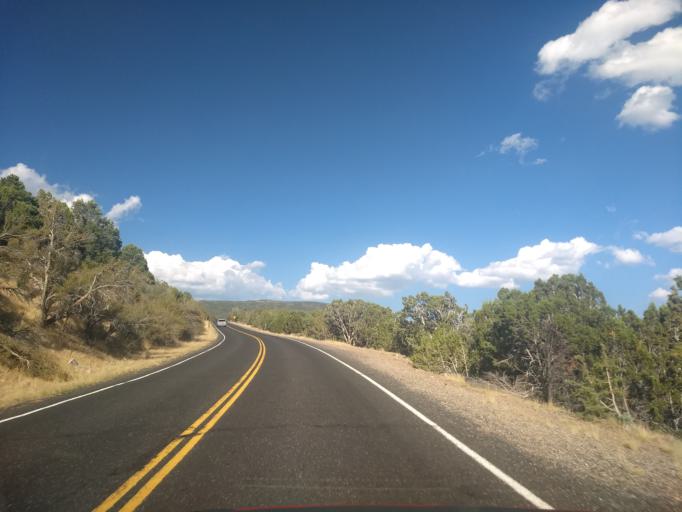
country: US
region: Utah
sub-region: Washington County
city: Enterprise
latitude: 37.4162
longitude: -113.5648
